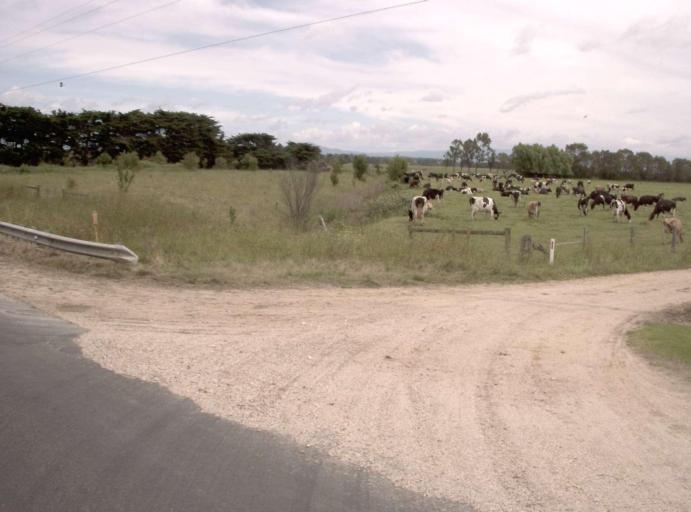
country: AU
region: Victoria
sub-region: Wellington
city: Sale
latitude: -37.9795
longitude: 147.0507
